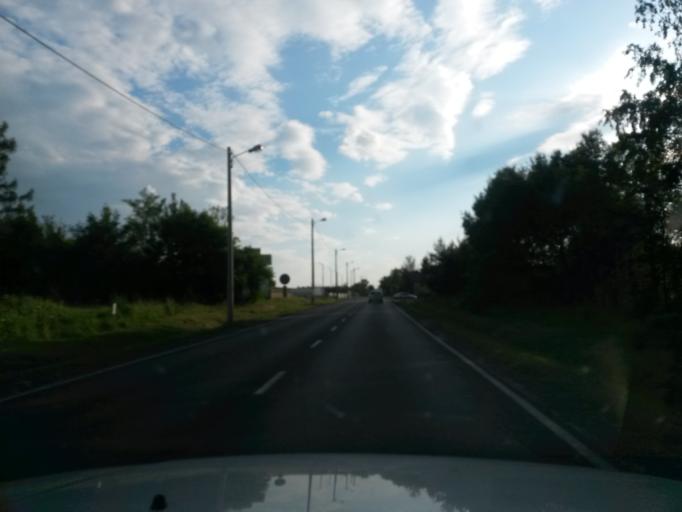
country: PL
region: Lodz Voivodeship
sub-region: Powiat belchatowski
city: Belchatow
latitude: 51.3553
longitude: 19.3358
